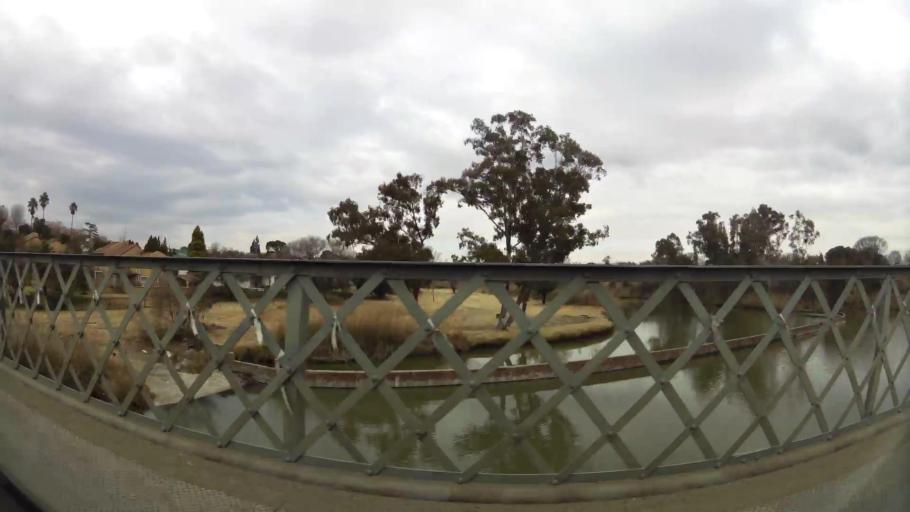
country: ZA
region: Orange Free State
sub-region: Fezile Dabi District Municipality
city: Kroonstad
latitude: -27.6705
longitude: 27.2322
